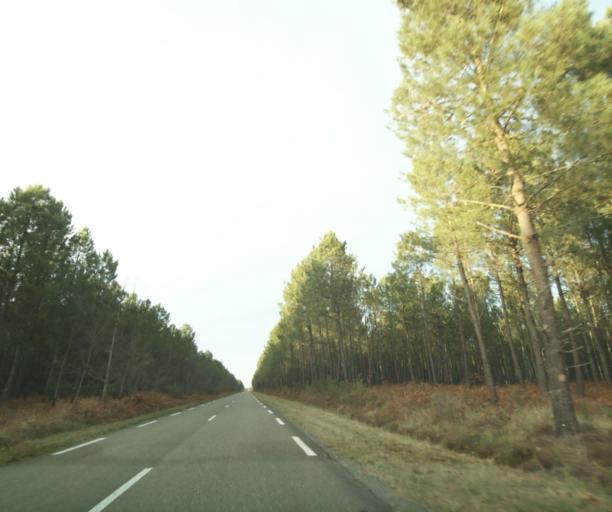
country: FR
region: Aquitaine
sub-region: Departement des Landes
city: Gabarret
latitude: 44.1370
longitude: -0.1182
